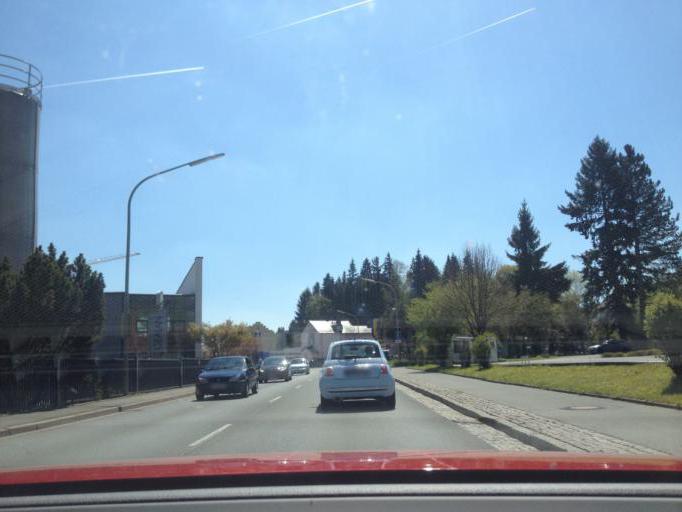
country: DE
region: Bavaria
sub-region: Upper Franconia
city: Oberkotzau
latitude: 50.2694
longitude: 11.9266
